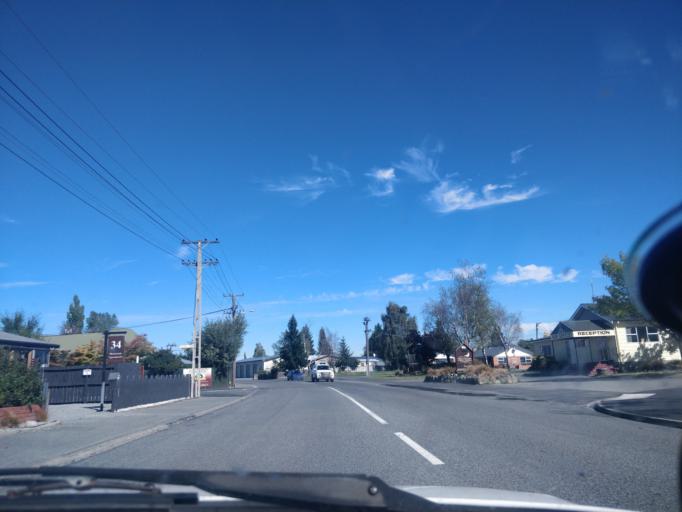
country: NZ
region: Canterbury
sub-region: Timaru District
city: Pleasant Point
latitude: -44.2590
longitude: 170.0988
